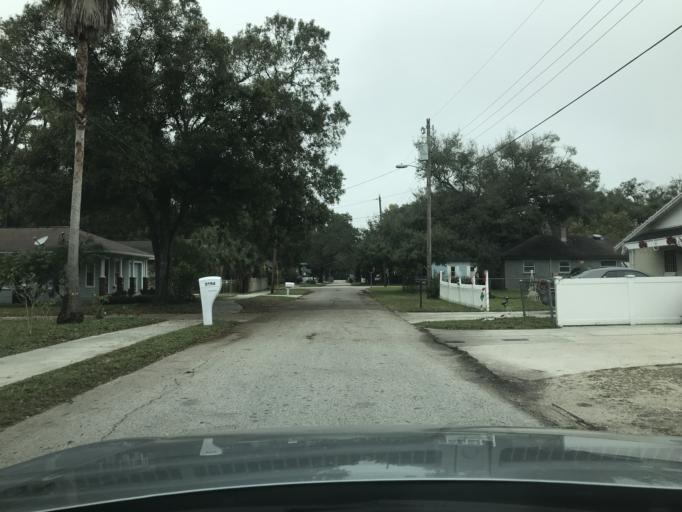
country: US
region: Florida
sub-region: Hillsborough County
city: Tampa
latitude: 27.9791
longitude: -82.4646
